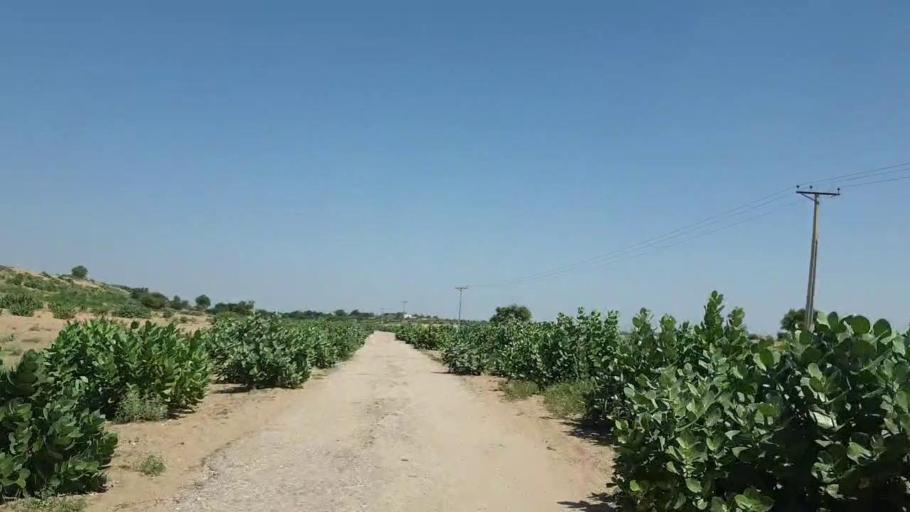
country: PK
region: Sindh
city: Islamkot
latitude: 25.1479
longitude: 70.4053
